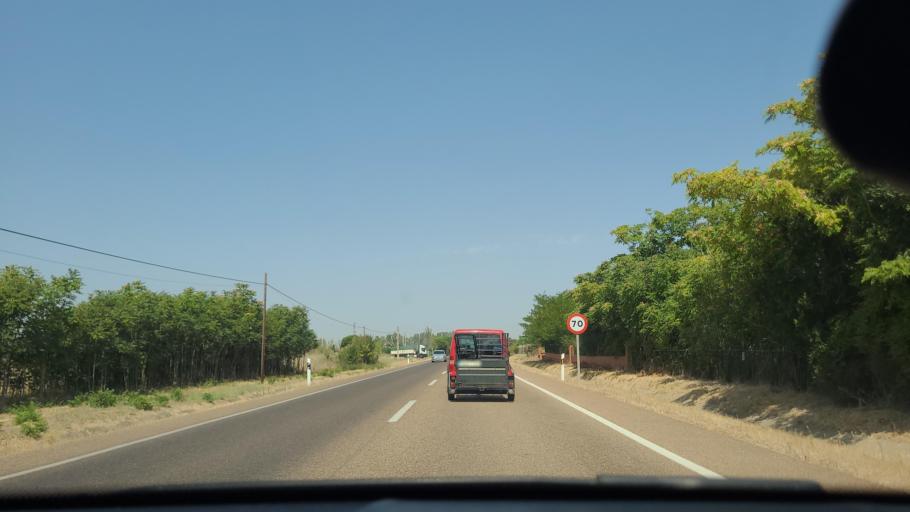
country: ES
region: Extremadura
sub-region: Provincia de Badajoz
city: Badajoz
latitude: 38.8306
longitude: -6.9178
